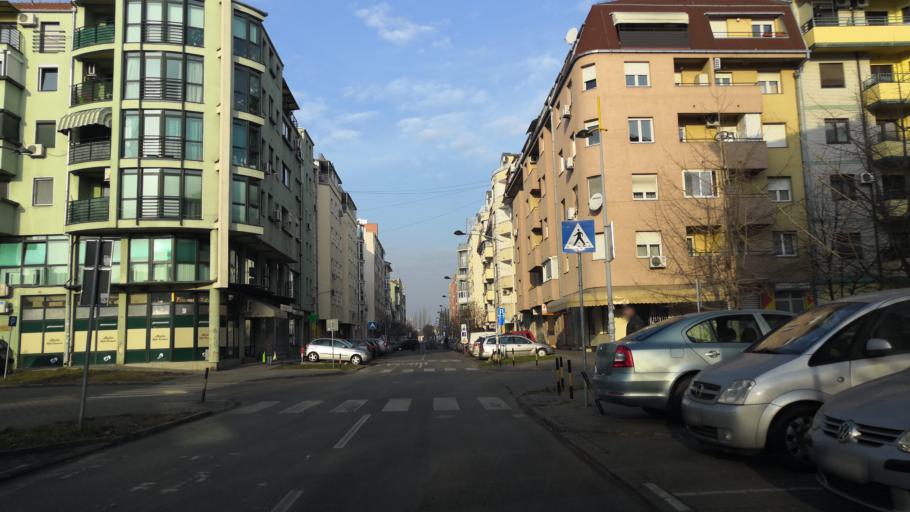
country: RS
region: Autonomna Pokrajina Vojvodina
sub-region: Juznobacki Okrug
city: Novi Sad
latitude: 45.2446
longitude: 19.8339
